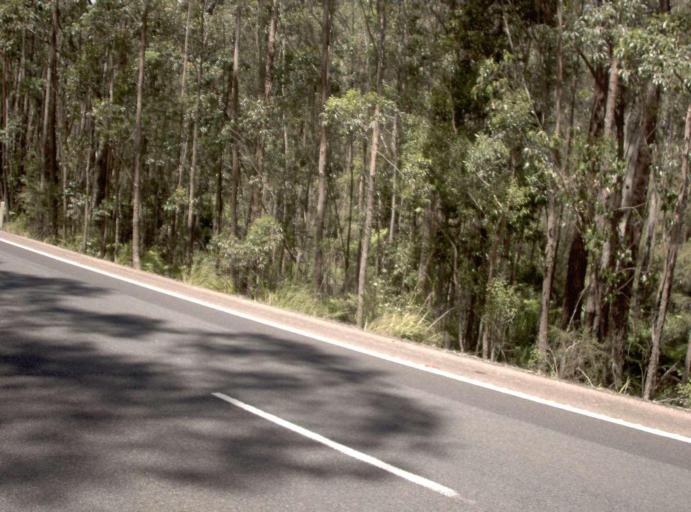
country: AU
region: New South Wales
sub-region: Bombala
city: Bombala
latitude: -37.6115
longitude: 148.8905
